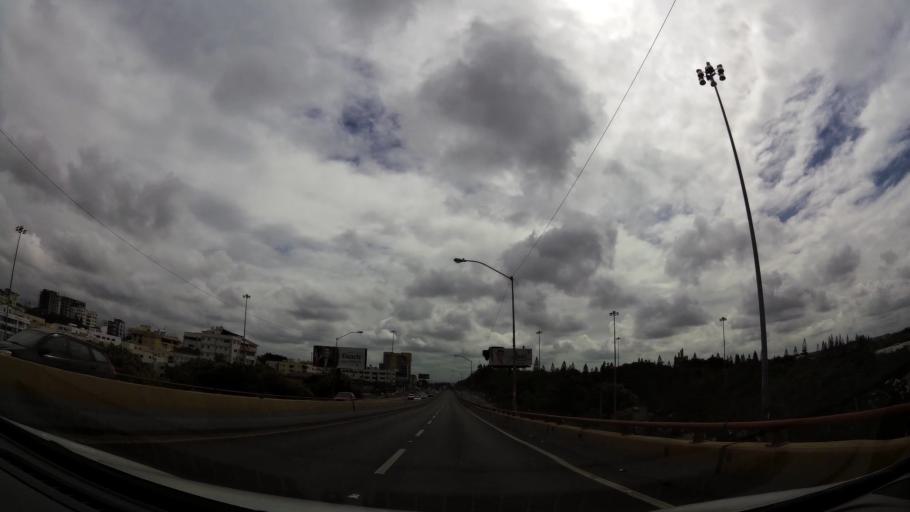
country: DO
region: Santiago
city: Santiago de los Caballeros
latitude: 19.4496
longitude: -70.6855
